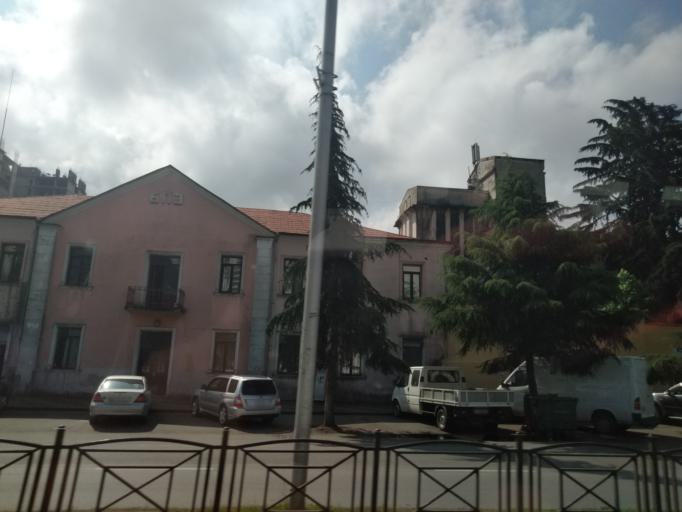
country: GE
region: Ajaria
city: Batumi
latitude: 41.6352
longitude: 41.6157
